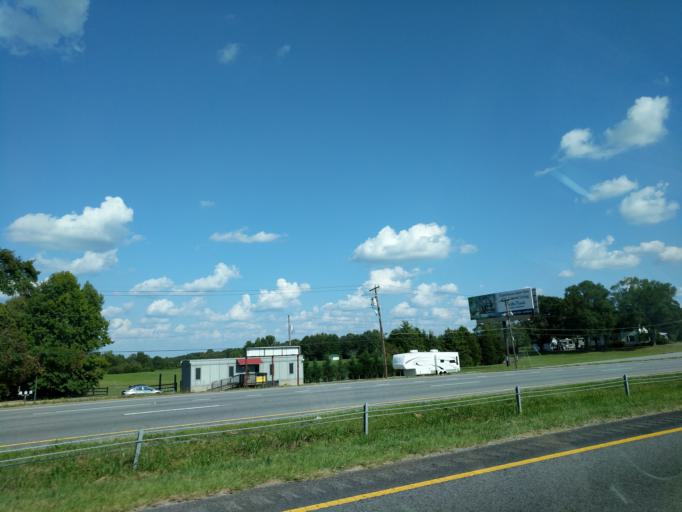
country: US
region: South Carolina
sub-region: Greenville County
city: Fountain Inn
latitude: 34.6643
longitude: -82.1757
